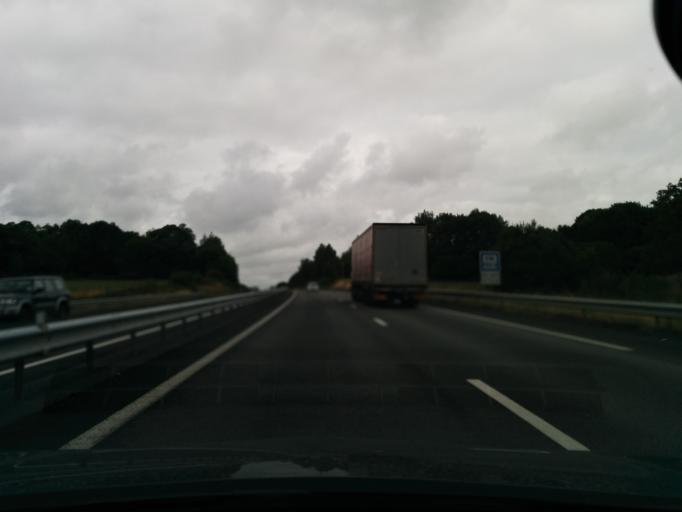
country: FR
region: Limousin
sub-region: Departement de la Haute-Vienne
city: Saint-Germain-les-Belles
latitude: 45.5565
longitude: 1.5047
